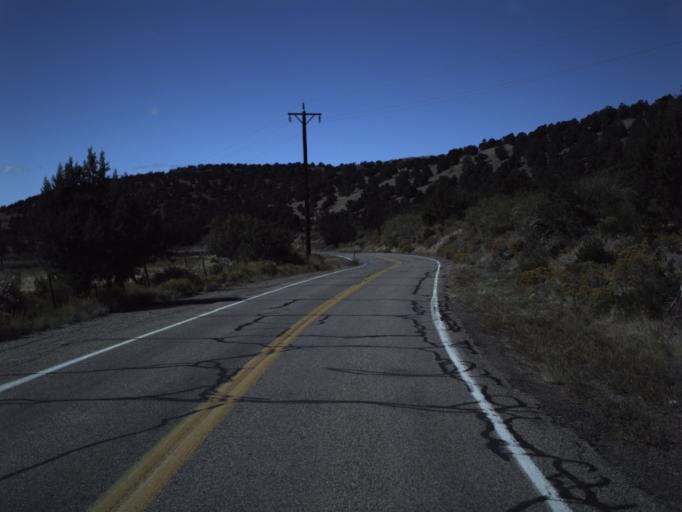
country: US
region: Utah
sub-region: Beaver County
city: Beaver
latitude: 38.2814
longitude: -112.5792
